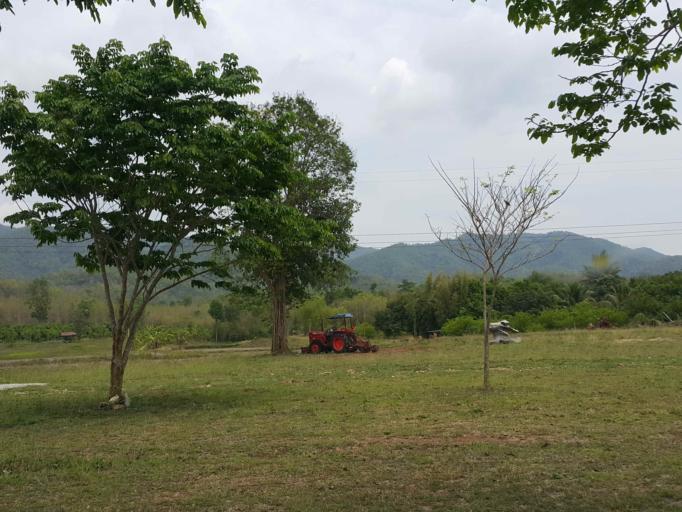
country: TH
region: Lampang
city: Thoen
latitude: 17.7347
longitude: 99.2337
